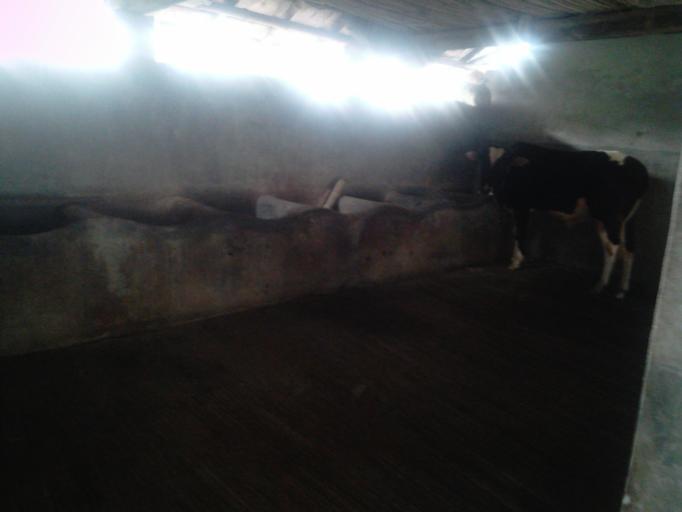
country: BD
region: Khulna
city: Kesabpur
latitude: 22.7709
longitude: 89.2522
